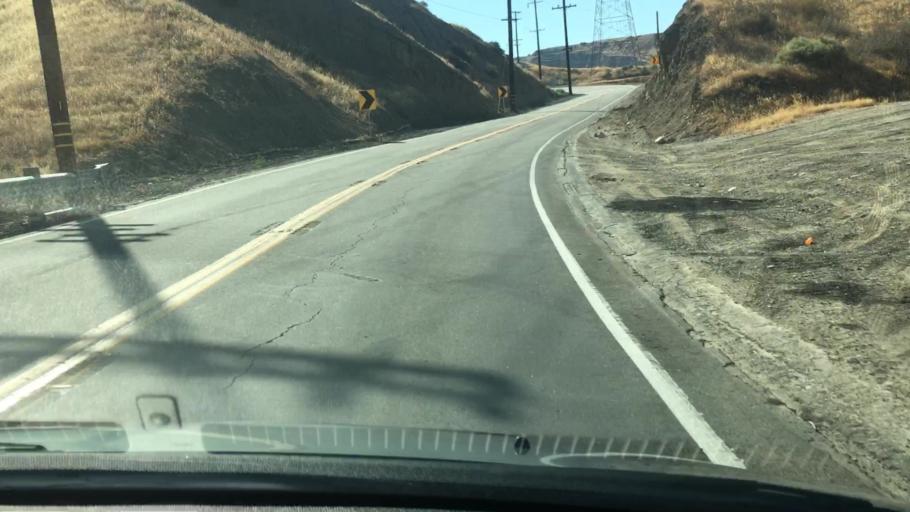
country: US
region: California
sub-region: Los Angeles County
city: Agua Dulce
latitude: 34.4748
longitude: -118.4478
